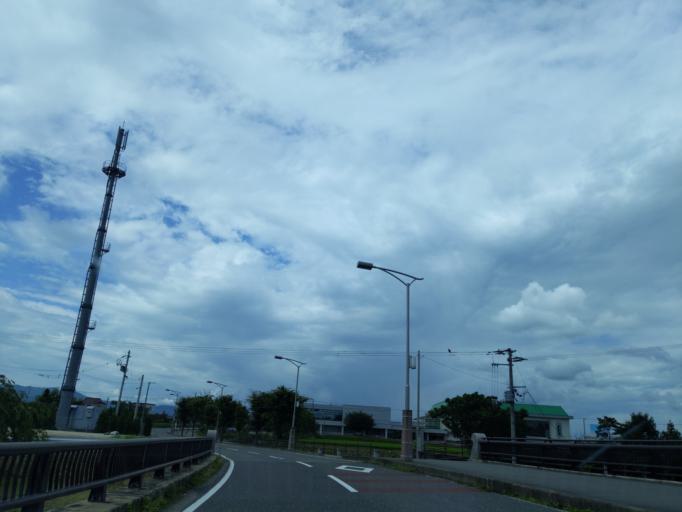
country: JP
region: Fukushima
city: Koriyama
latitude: 37.3636
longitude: 140.3535
